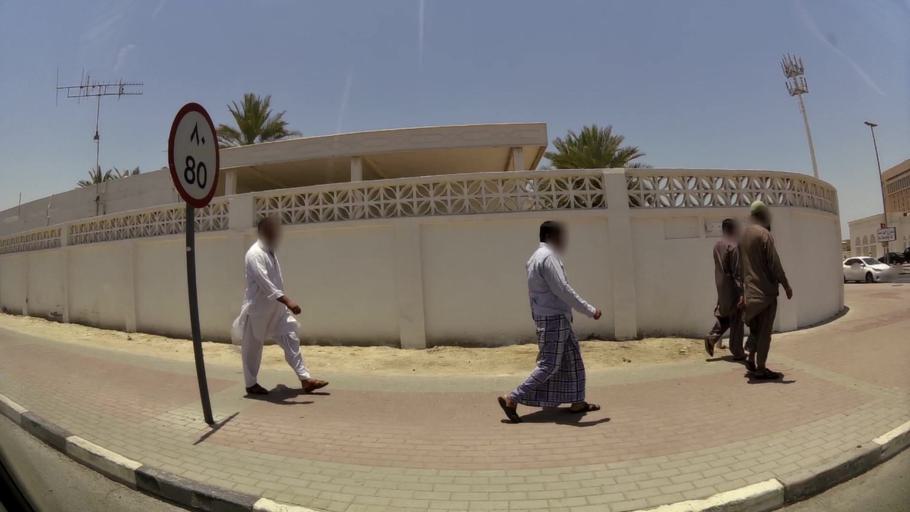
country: AE
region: Ash Shariqah
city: Sharjah
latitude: 25.2831
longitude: 55.3247
